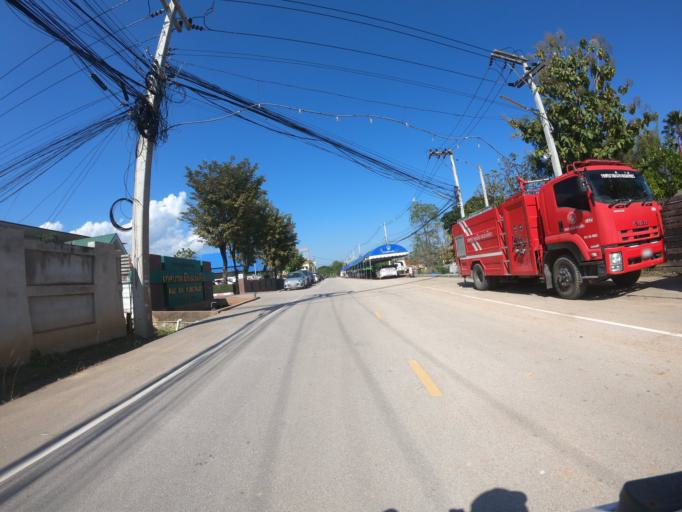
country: TH
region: Chiang Mai
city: Chiang Mai
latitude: 18.7429
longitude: 98.9645
